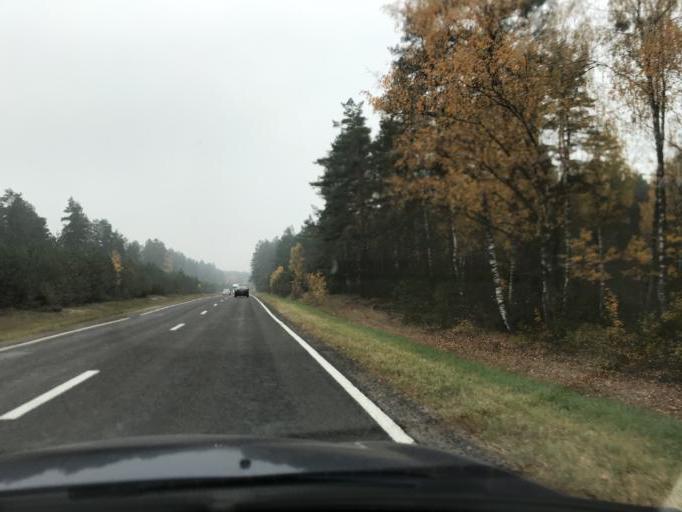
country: LT
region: Alytaus apskritis
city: Druskininkai
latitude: 53.8925
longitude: 23.9117
